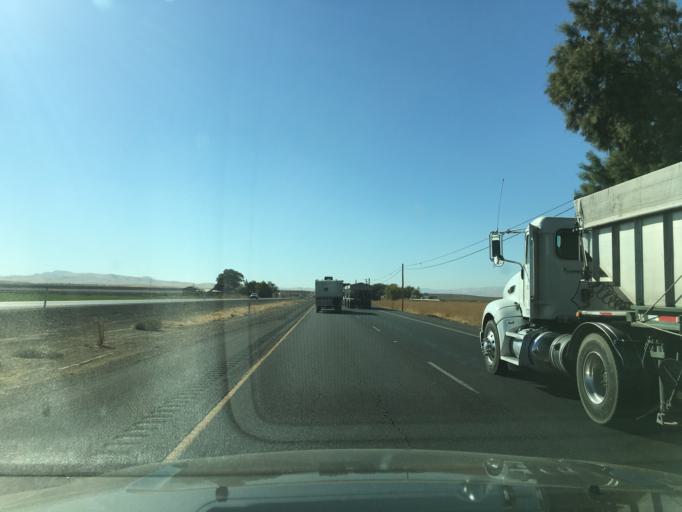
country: US
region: California
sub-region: Merced County
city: Los Banos
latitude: 37.0566
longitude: -120.9316
